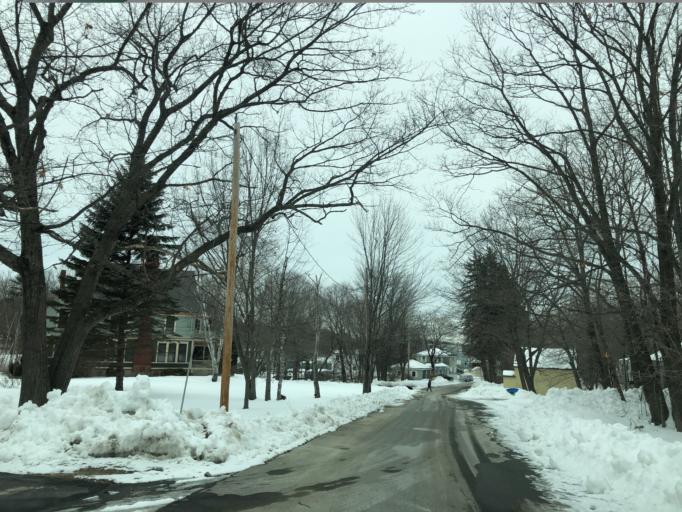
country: US
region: Maine
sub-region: Cumberland County
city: Westbrook
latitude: 43.6841
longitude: -70.3576
